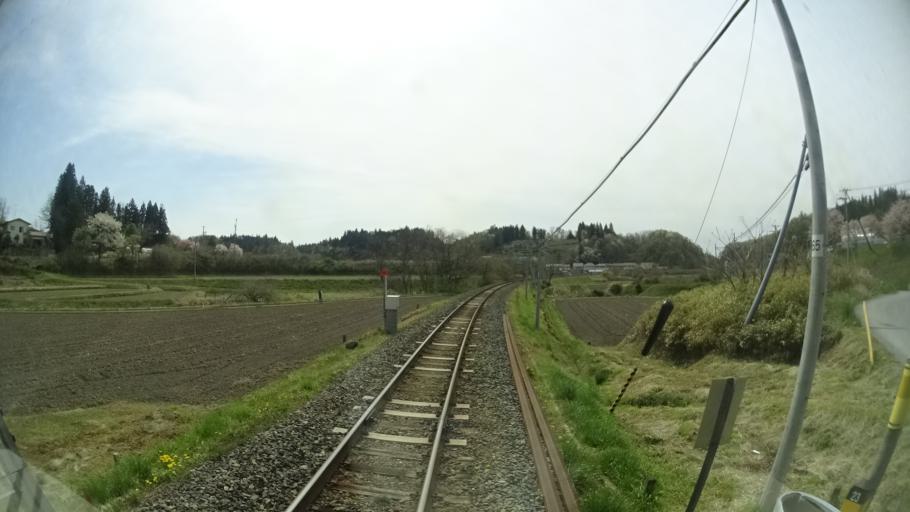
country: JP
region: Iwate
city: Ichinoseki
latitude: 38.9364
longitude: 141.3418
